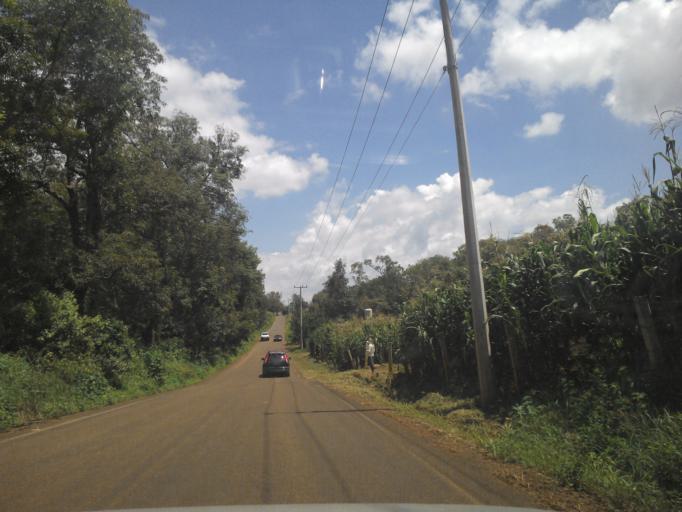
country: MX
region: Jalisco
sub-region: Atotonilco el Alto
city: Ojo de Agua de Moran
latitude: 20.6022
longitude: -102.4843
